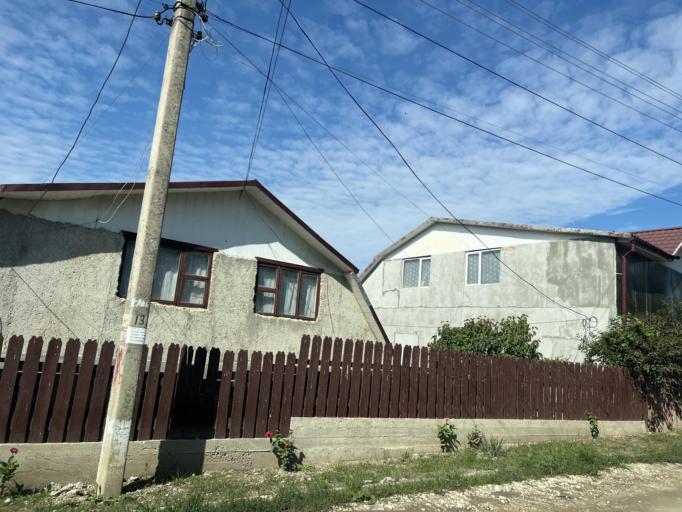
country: MD
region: Ungheni
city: Ungheni
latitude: 47.2021
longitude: 27.8109
